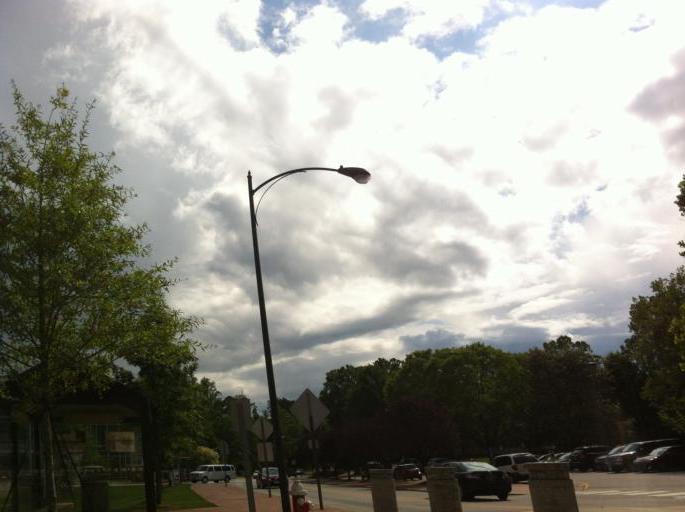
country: US
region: North Carolina
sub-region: Wake County
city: West Raleigh
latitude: 35.7857
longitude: -78.6752
